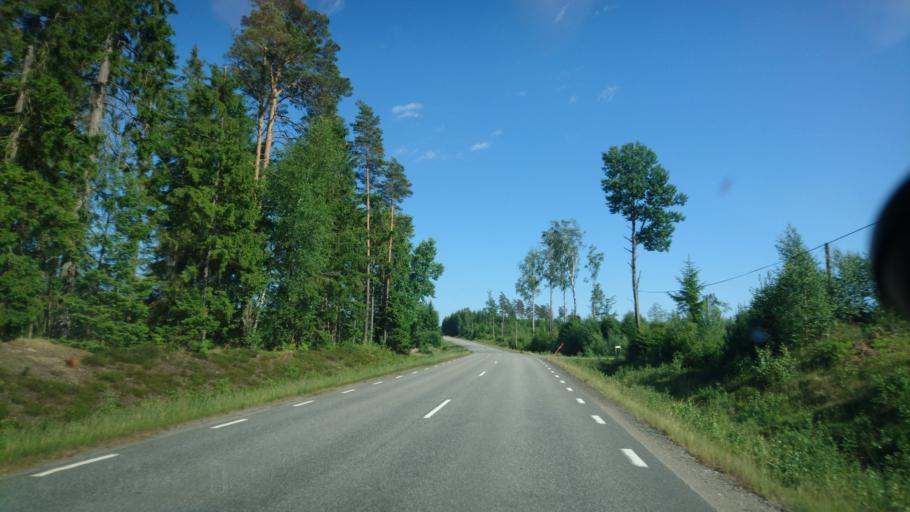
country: SE
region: Skane
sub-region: Osby Kommun
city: Lonsboda
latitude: 56.4276
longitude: 14.2721
